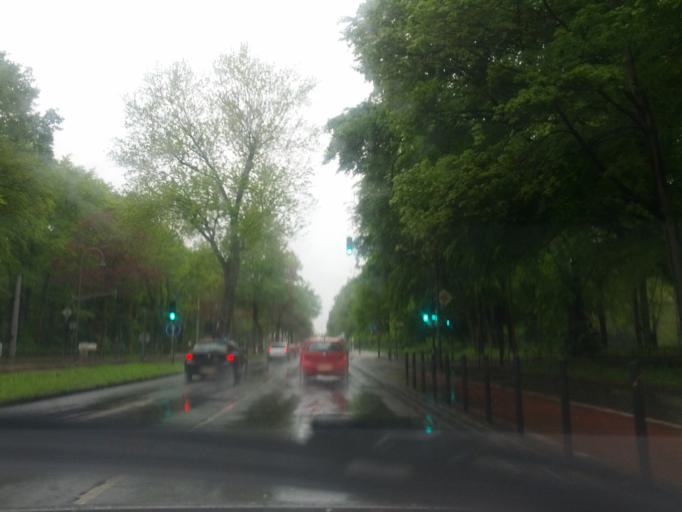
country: DE
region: North Rhine-Westphalia
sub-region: Regierungsbezirk Koln
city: Mengenich
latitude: 50.9378
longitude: 6.8714
